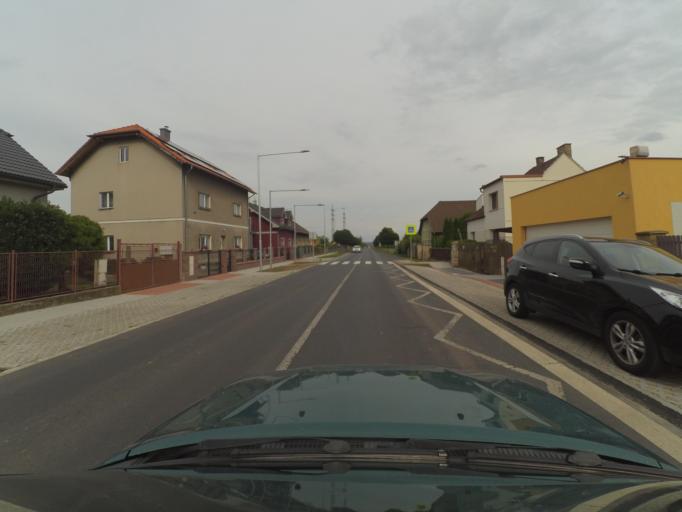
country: CZ
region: Ustecky
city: Cerncice
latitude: 50.3602
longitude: 13.8314
